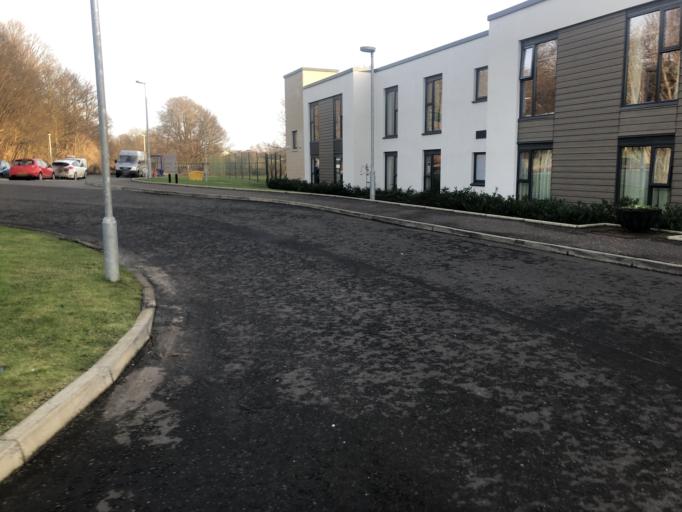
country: GB
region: Scotland
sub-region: Edinburgh
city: Colinton
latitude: 55.9408
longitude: -3.2663
